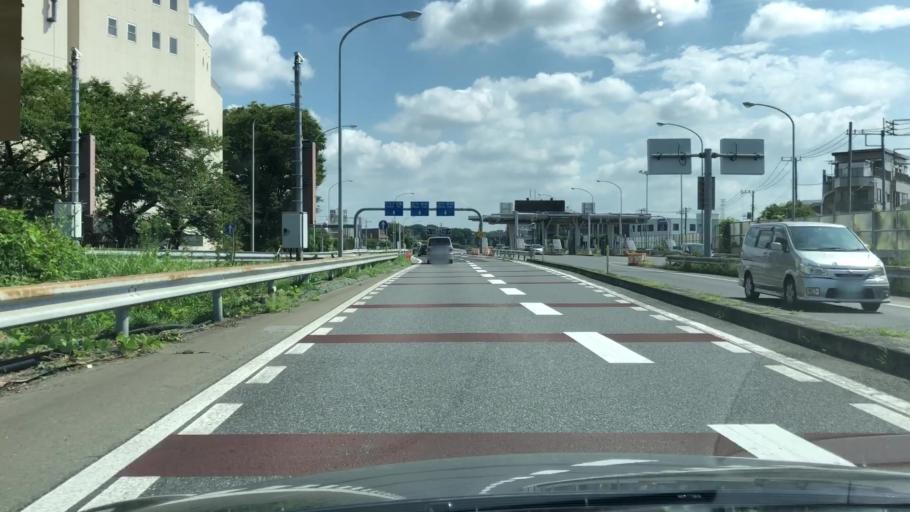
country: JP
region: Tokyo
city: Hino
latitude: 35.6733
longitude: 139.4412
